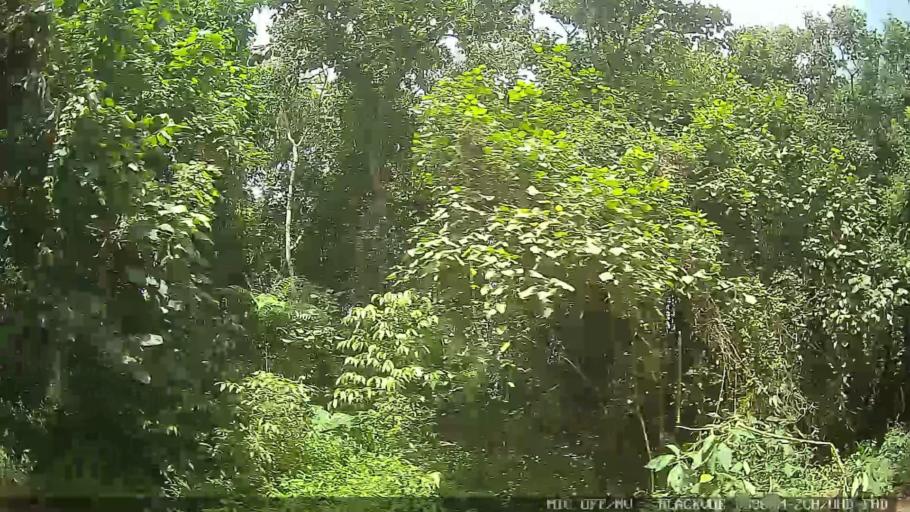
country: BR
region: Sao Paulo
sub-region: Rio Grande Da Serra
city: Rio Grande da Serra
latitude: -23.6980
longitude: -46.2790
